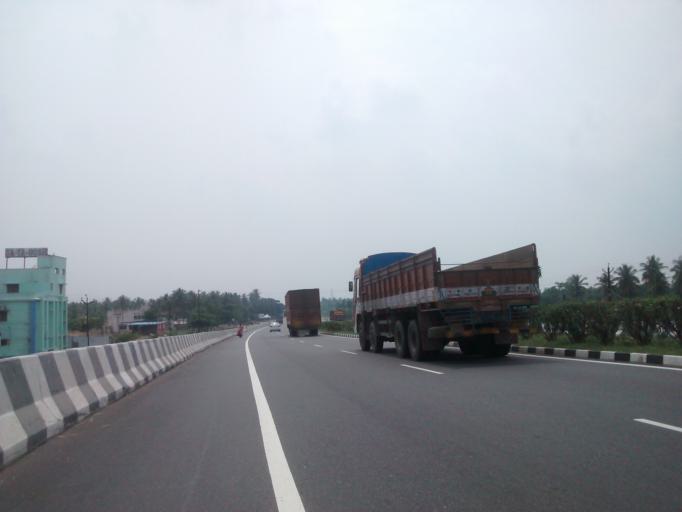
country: IN
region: Tamil Nadu
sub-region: Dharmapuri
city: Dharmapuri
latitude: 12.2428
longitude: 78.1952
